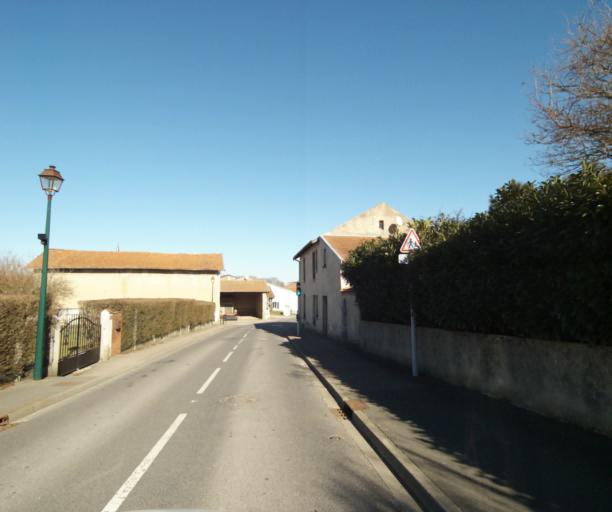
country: FR
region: Lorraine
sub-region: Departement de Meurthe-et-Moselle
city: Fleville-devant-Nancy
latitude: 48.6236
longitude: 6.2023
